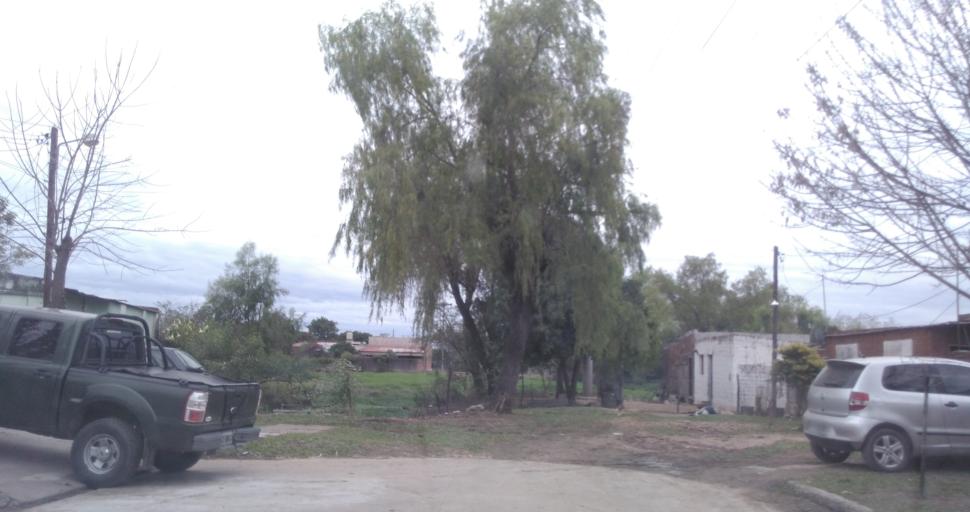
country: AR
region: Chaco
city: Resistencia
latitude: -27.4716
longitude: -58.9665
